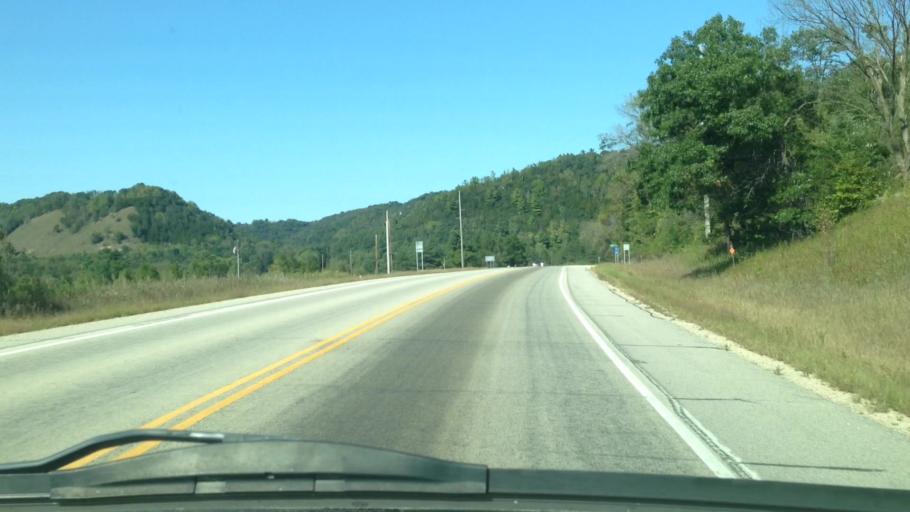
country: US
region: Minnesota
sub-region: Fillmore County
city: Rushford
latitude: 43.8309
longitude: -91.7664
